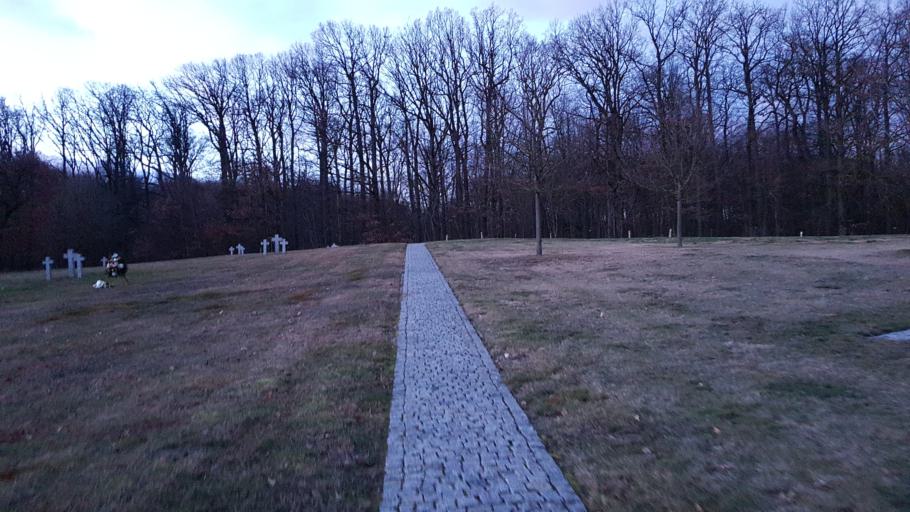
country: PL
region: West Pomeranian Voivodeship
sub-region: Powiat gryfinski
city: Stare Czarnowo
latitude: 53.2960
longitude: 14.7260
